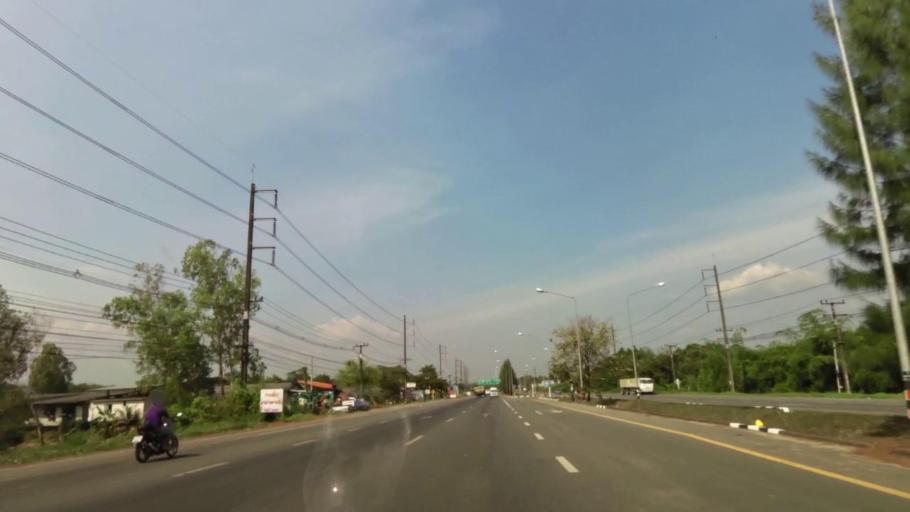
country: TH
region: Chanthaburi
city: Chanthaburi
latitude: 12.6451
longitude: 102.1303
